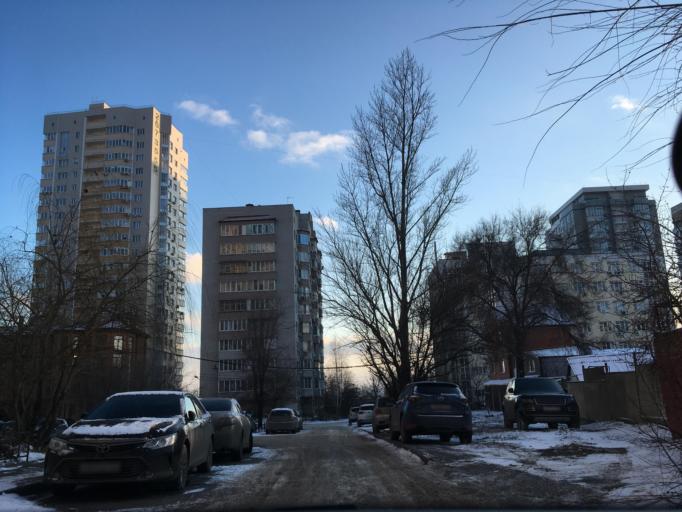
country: RU
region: Rostov
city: Rostov-na-Donu
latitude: 47.2255
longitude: 39.7498
